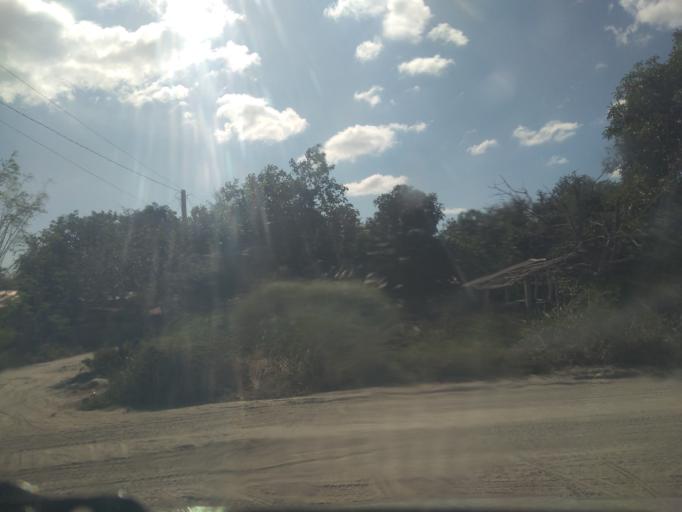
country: PH
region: Central Luzon
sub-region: Province of Pampanga
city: Balas
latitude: 15.0760
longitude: 120.6029
